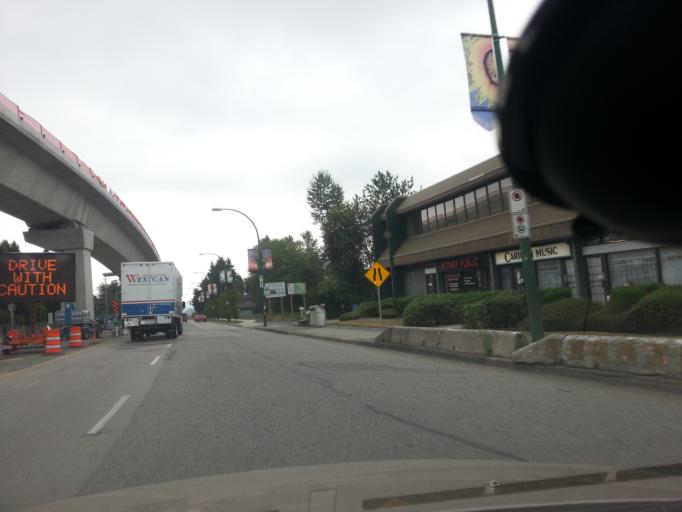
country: CA
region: British Columbia
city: Port Moody
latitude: 49.2587
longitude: -122.8931
